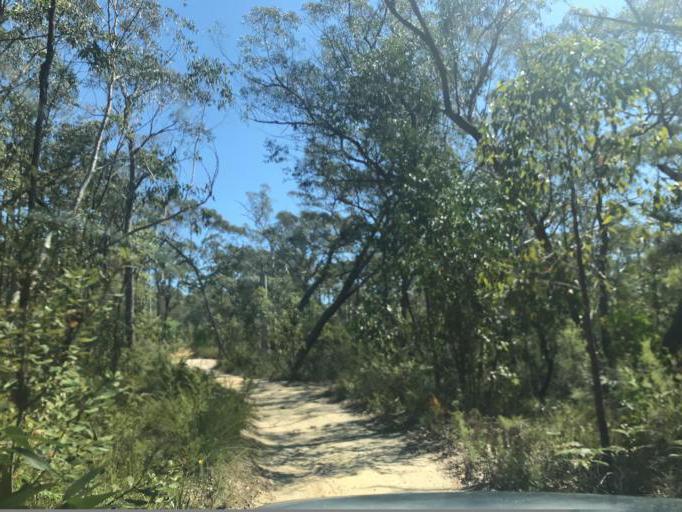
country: AU
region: New South Wales
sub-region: Wyong Shire
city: Little Jilliby
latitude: -33.1476
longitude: 151.1001
